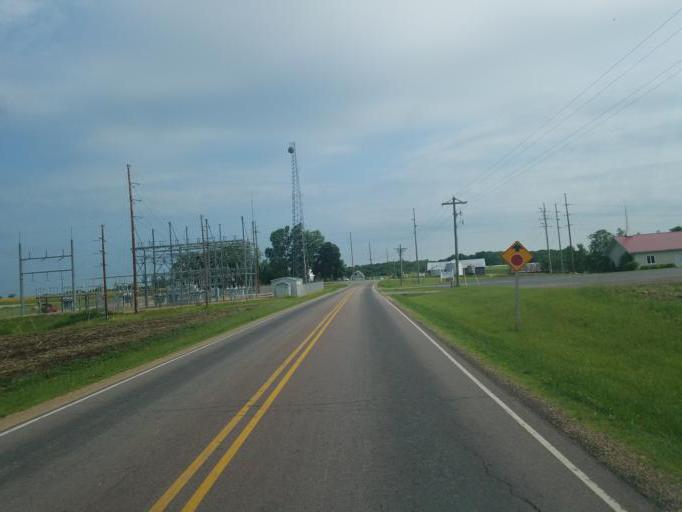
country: US
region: Wisconsin
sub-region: Vernon County
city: Hillsboro
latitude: 43.6660
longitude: -90.4588
